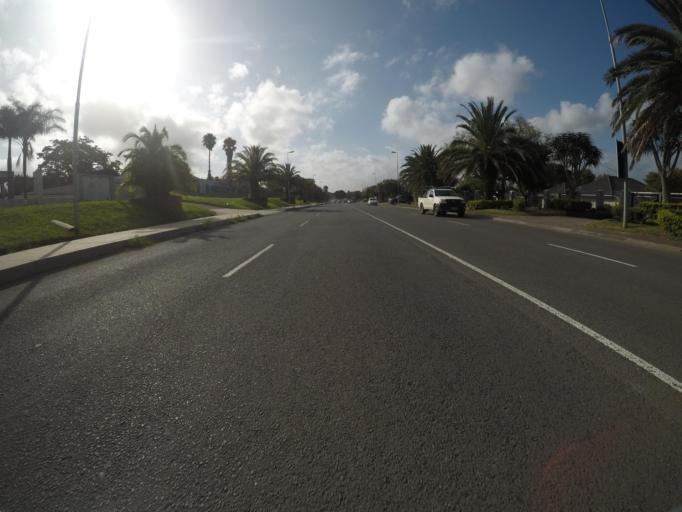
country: ZA
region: Eastern Cape
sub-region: Buffalo City Metropolitan Municipality
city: East London
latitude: -32.9655
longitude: 27.9369
